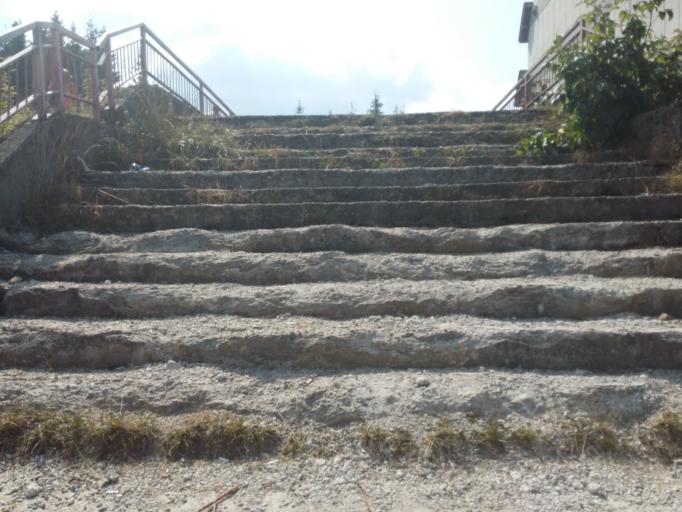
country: RO
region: Valcea
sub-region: Comuna Voineasa
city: Voineasa
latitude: 45.4296
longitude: 23.7541
